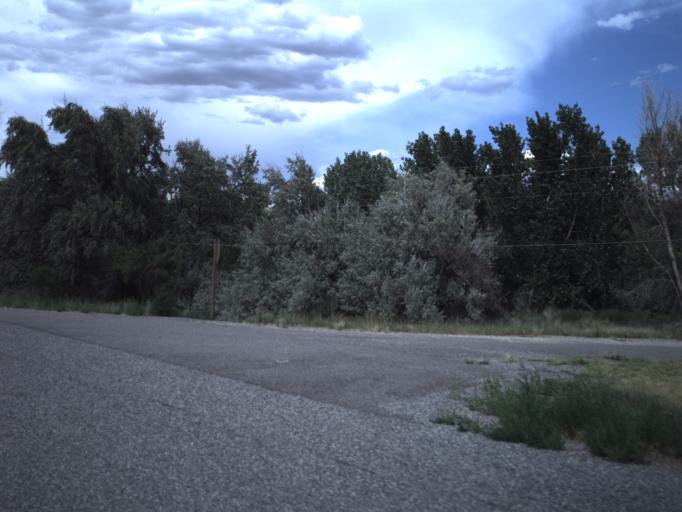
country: US
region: Utah
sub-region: Sevier County
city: Salina
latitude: 38.9429
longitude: -111.8547
